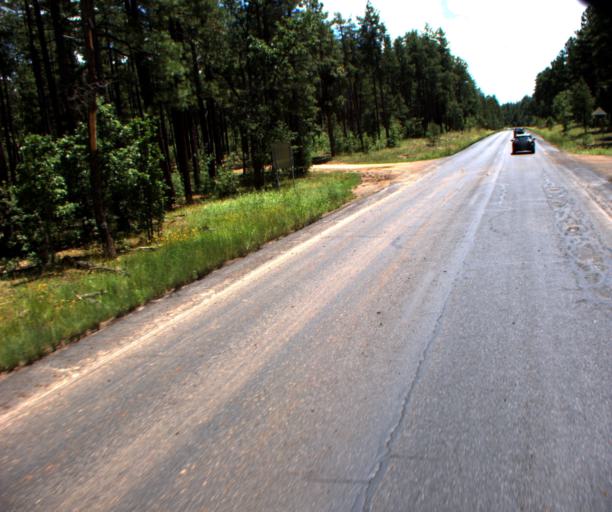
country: US
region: Arizona
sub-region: Gila County
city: Pine
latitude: 34.4720
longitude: -111.4494
